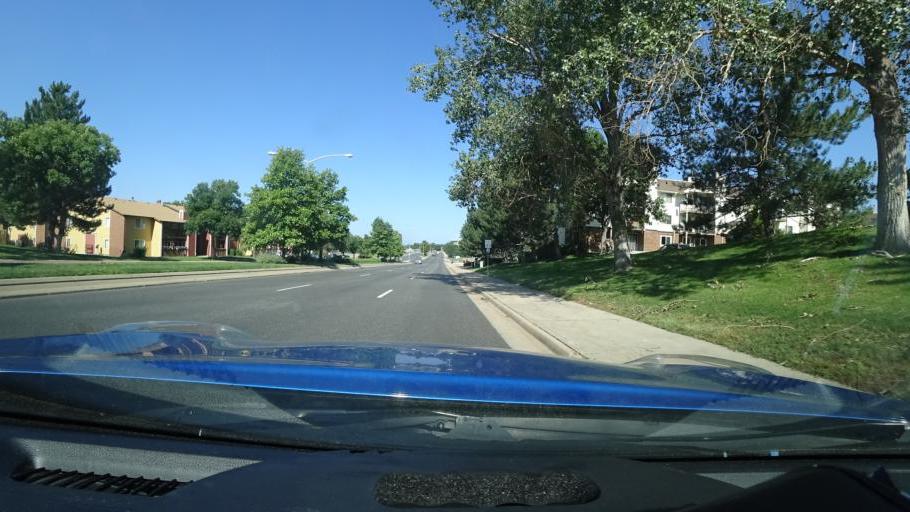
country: US
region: Colorado
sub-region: Adams County
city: Aurora
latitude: 39.7074
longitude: -104.8018
